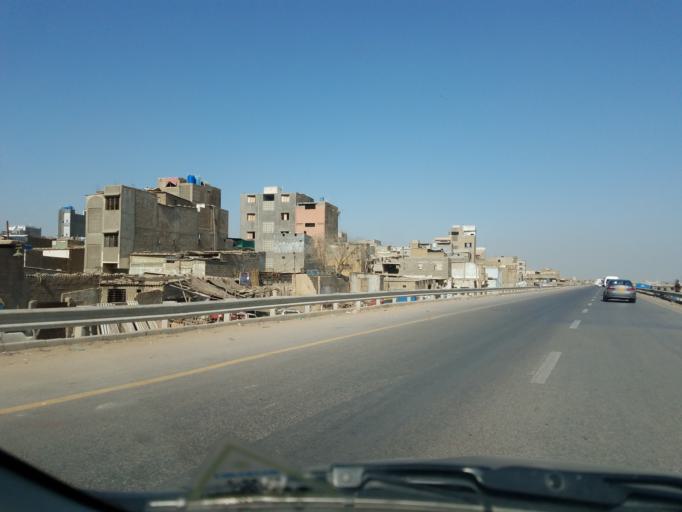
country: PK
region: Sindh
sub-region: Karachi District
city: Karachi
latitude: 24.8784
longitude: 66.9871
